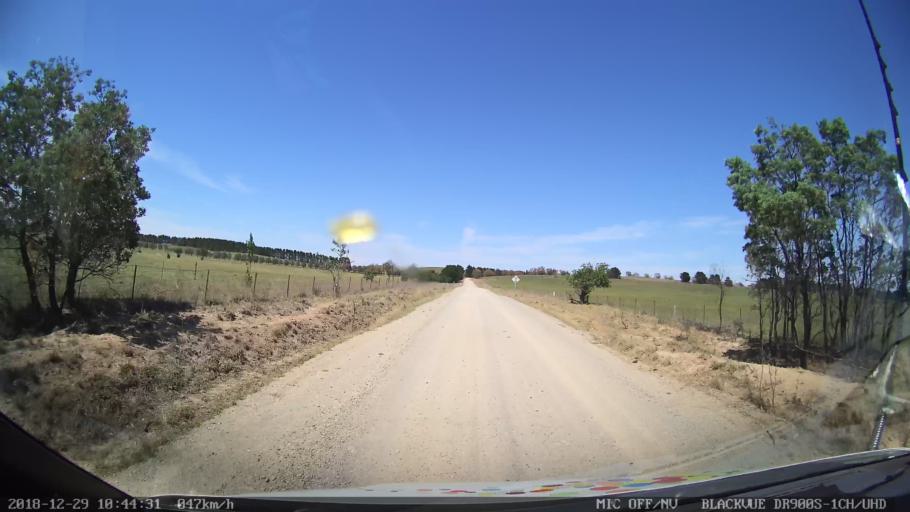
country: AU
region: New South Wales
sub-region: Palerang
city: Bungendore
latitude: -35.0421
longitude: 149.5278
